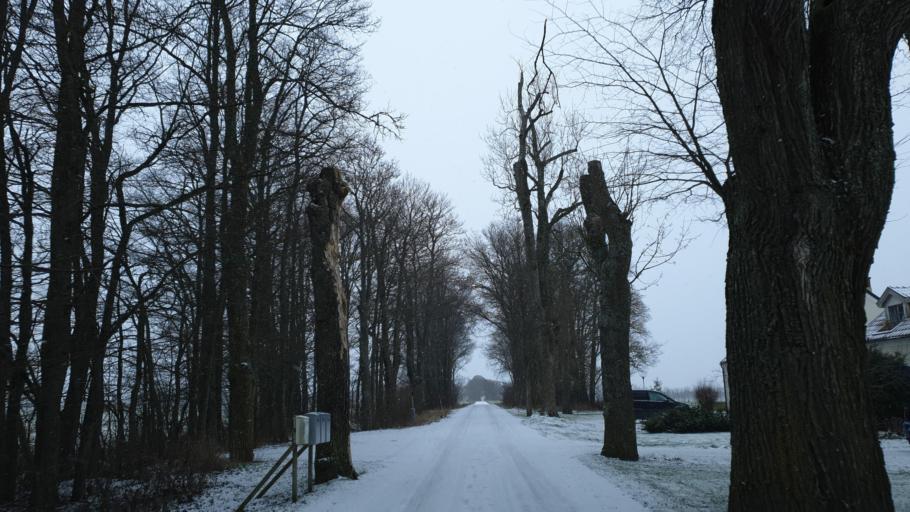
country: SE
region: Gotland
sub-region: Gotland
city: Visby
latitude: 57.5207
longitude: 18.4527
